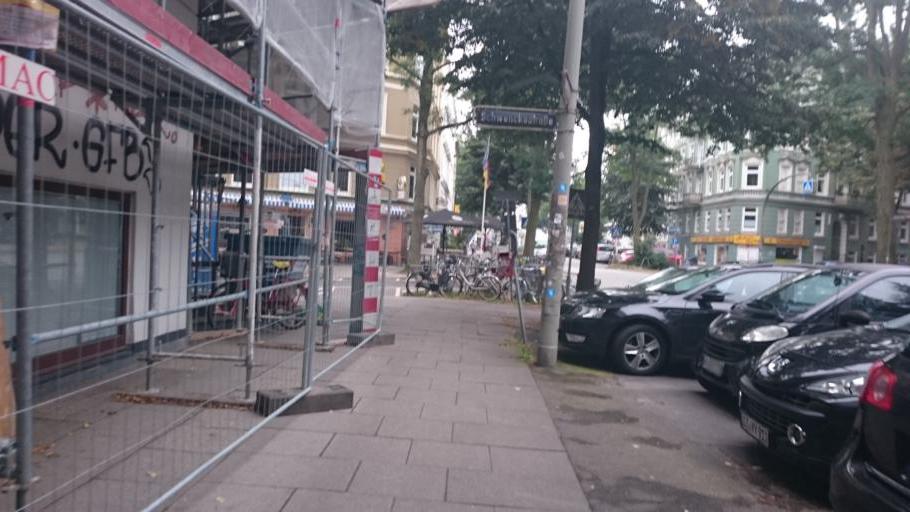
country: DE
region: Hamburg
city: Stellingen
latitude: 53.5789
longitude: 9.9500
